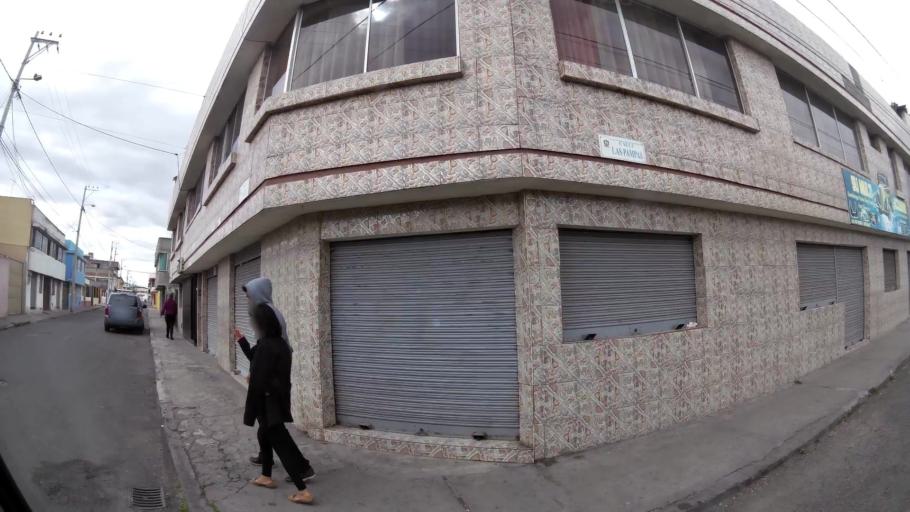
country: EC
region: Cotopaxi
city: Latacunga
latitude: -0.9324
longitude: -78.6249
